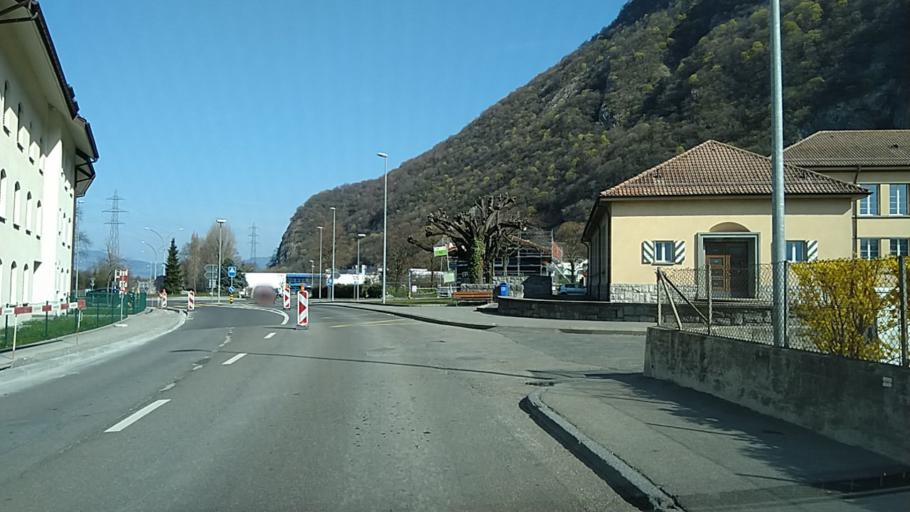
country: CH
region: Vaud
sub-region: Aigle District
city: Villeneuve
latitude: 46.3612
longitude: 6.9293
